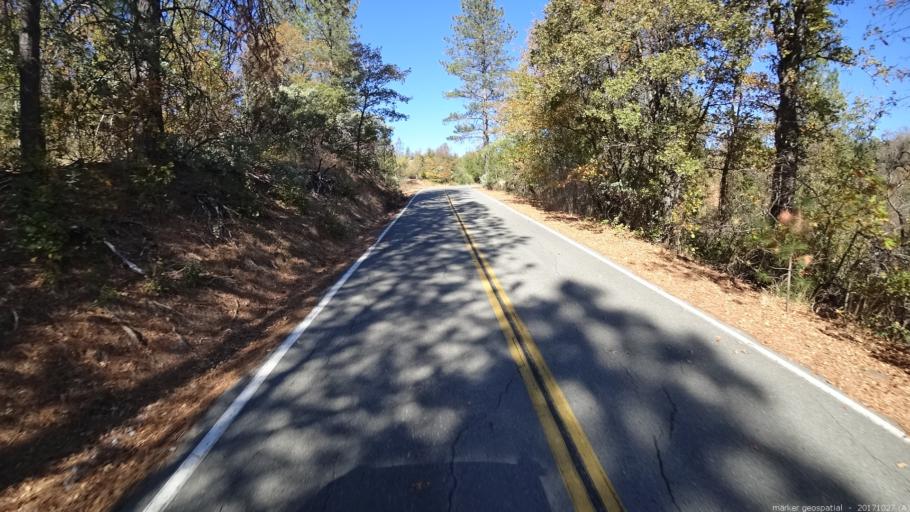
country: US
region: California
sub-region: Shasta County
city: Bella Vista
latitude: 40.7479
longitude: -121.9946
